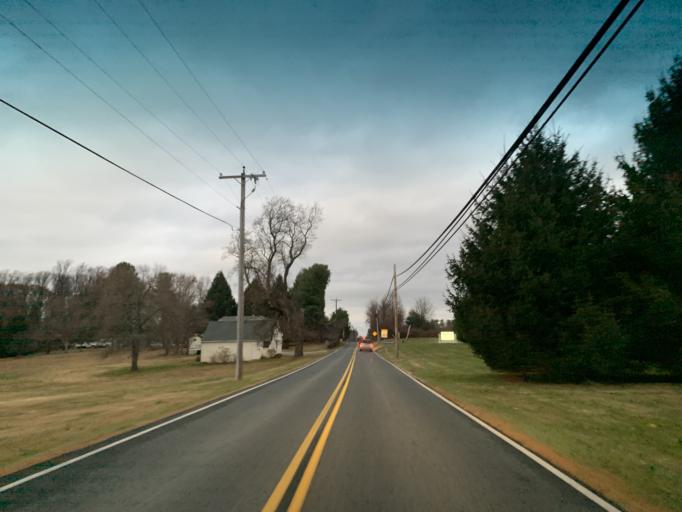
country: US
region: Maryland
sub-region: Harford County
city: Fallston
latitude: 39.5290
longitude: -76.4471
